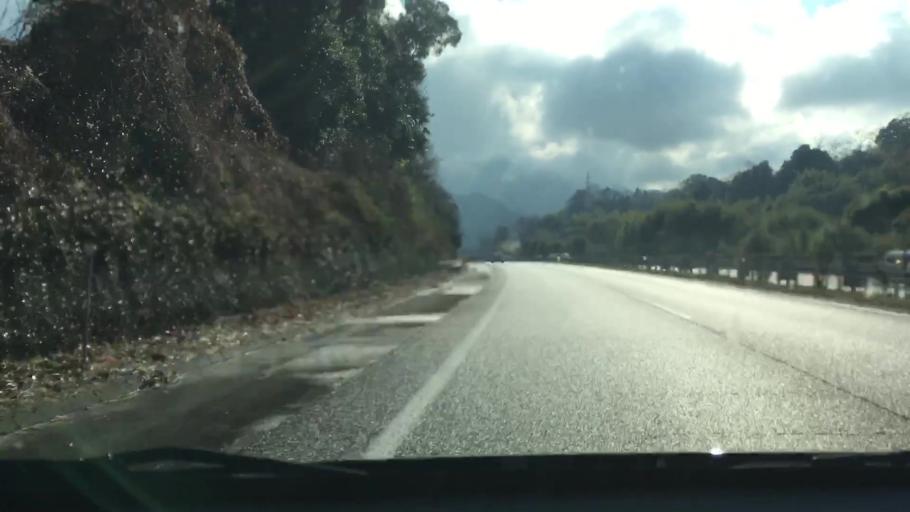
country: JP
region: Kumamoto
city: Matsubase
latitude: 32.5584
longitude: 130.6960
